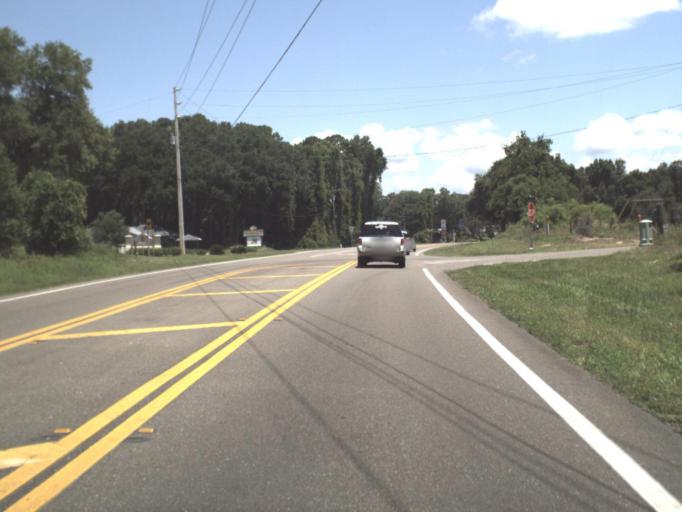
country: US
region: Florida
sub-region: Clay County
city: Keystone Heights
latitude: 29.7524
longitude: -82.0562
